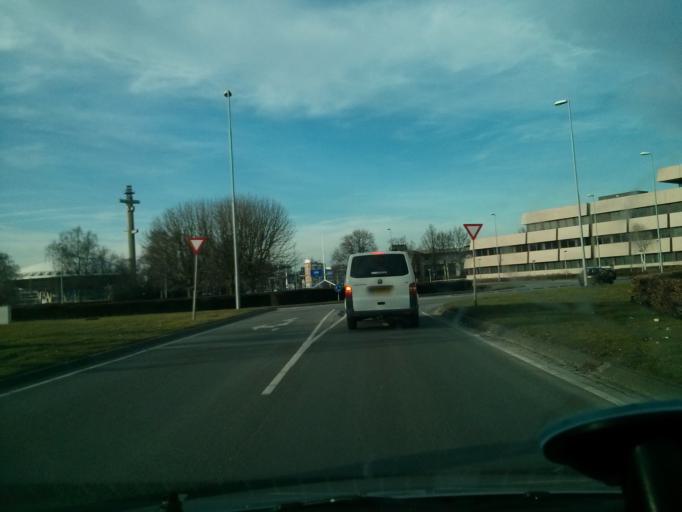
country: NL
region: North Brabant
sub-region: Gemeente Eindhoven
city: Eindhoven
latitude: 51.4405
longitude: 5.4501
